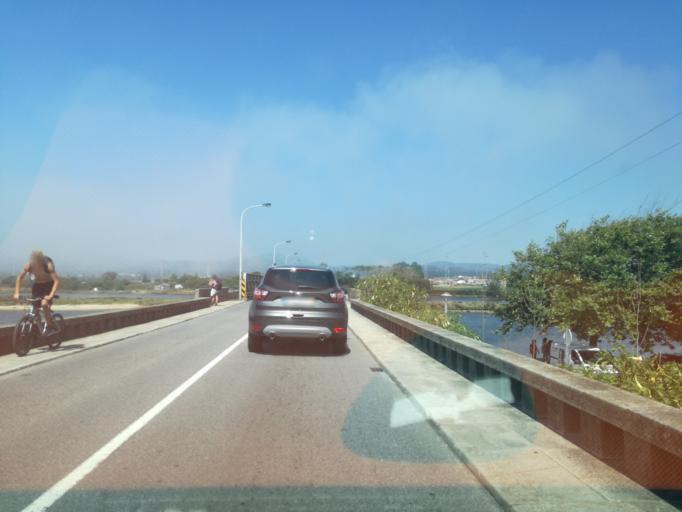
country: PT
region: Braga
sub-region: Esposende
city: Esposende
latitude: 41.5144
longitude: -8.7730
